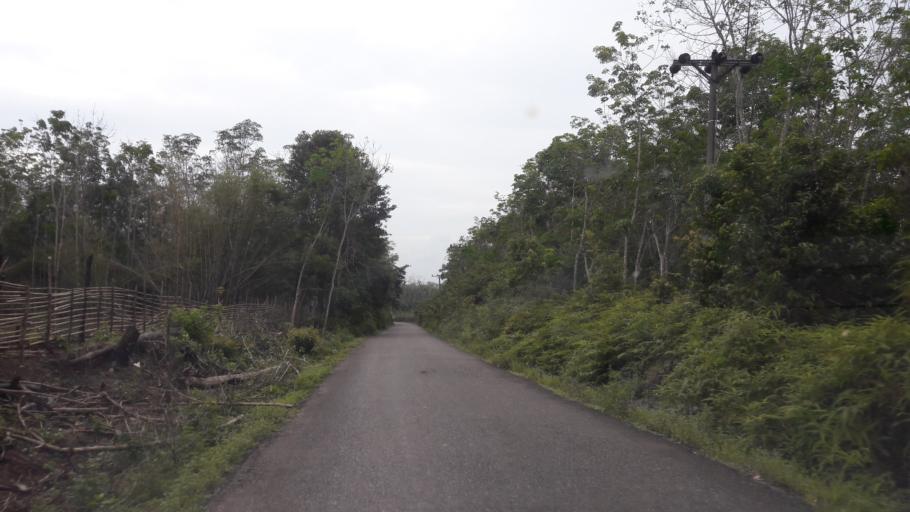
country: ID
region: South Sumatra
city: Gunungmenang
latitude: -3.1169
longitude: 104.0916
